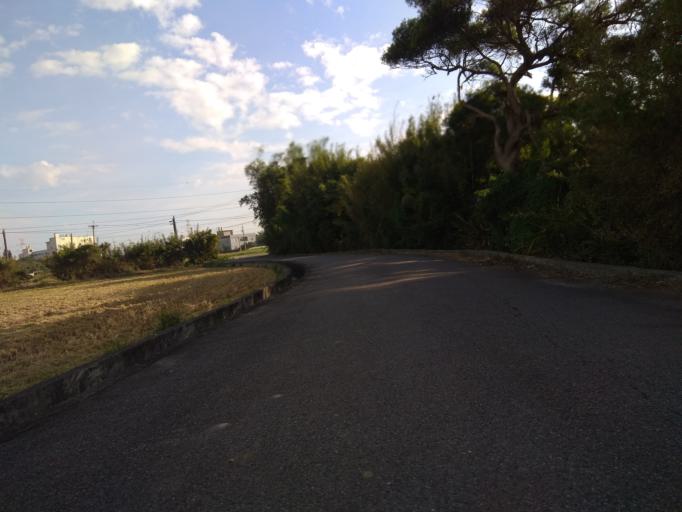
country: TW
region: Taiwan
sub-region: Hsinchu
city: Zhubei
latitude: 24.9777
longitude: 121.0625
